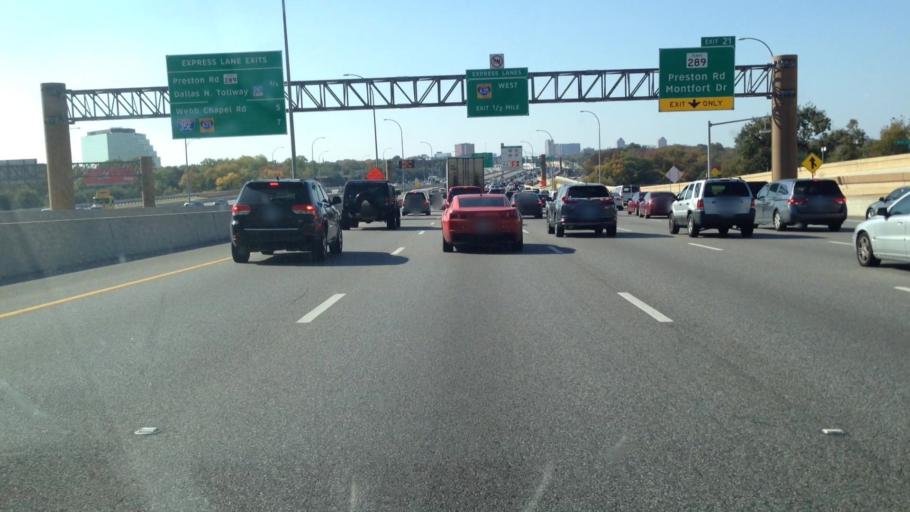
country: US
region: Texas
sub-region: Dallas County
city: Richardson
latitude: 32.9244
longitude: -96.7771
